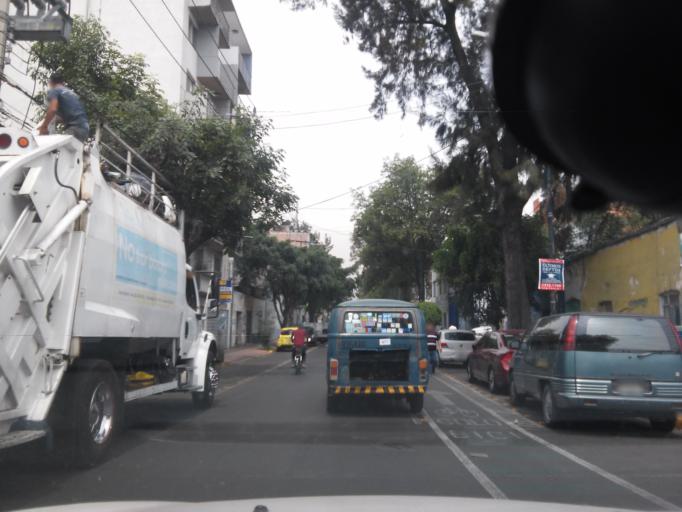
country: MX
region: Mexico City
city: Cuauhtemoc
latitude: 19.4441
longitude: -99.1719
